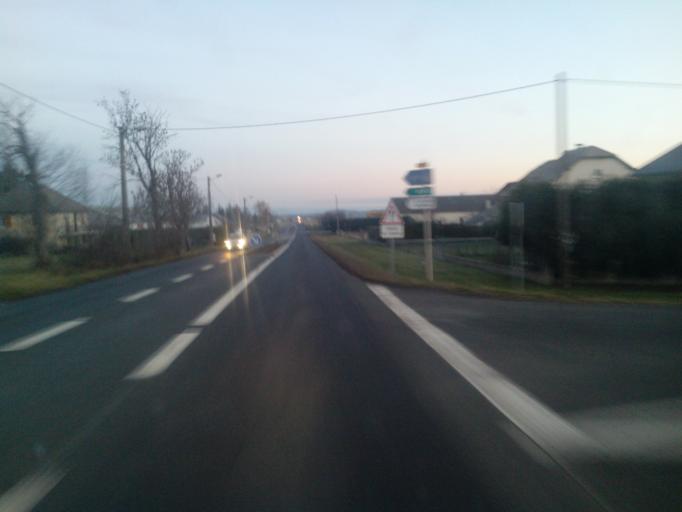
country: FR
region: Auvergne
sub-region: Departement du Cantal
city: Neussargues-Moissac
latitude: 45.0800
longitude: 2.9413
